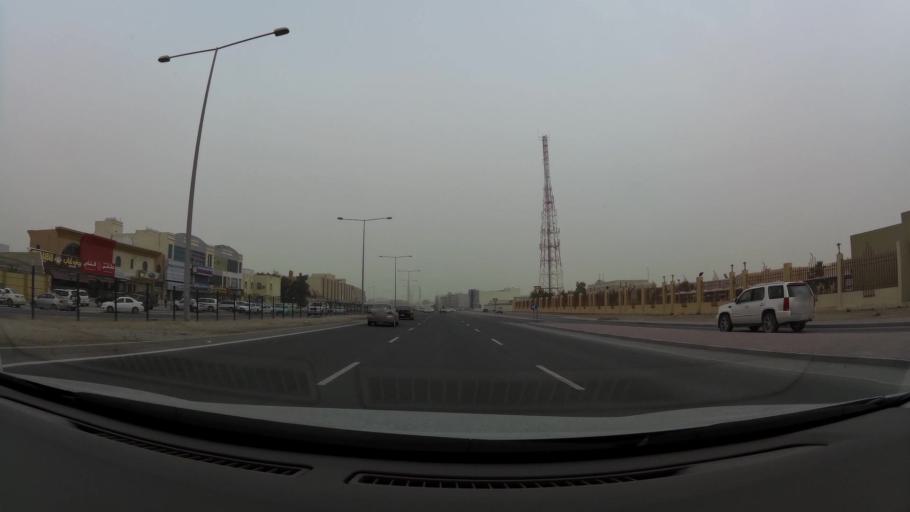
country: QA
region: Baladiyat ad Dawhah
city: Doha
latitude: 25.2323
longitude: 51.4855
